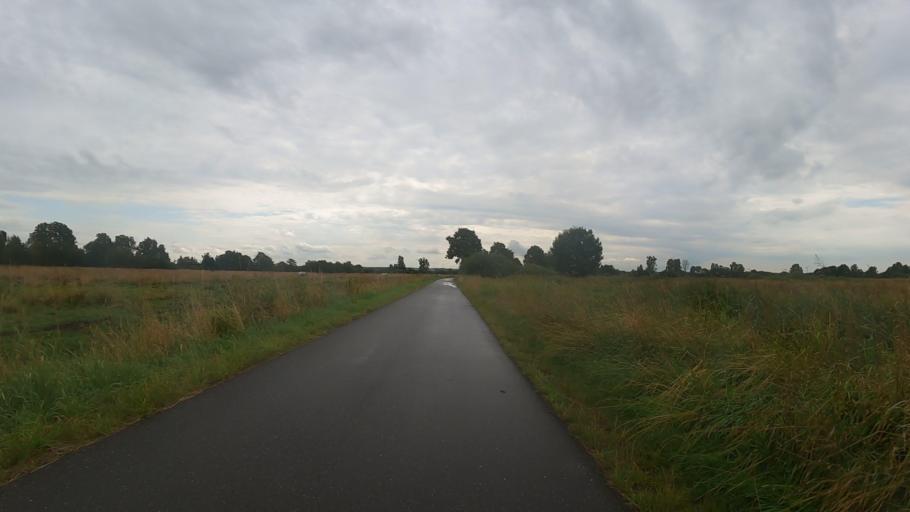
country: DE
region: Lower Saxony
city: Neu Wulmstorf
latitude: 53.4827
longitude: 9.7679
